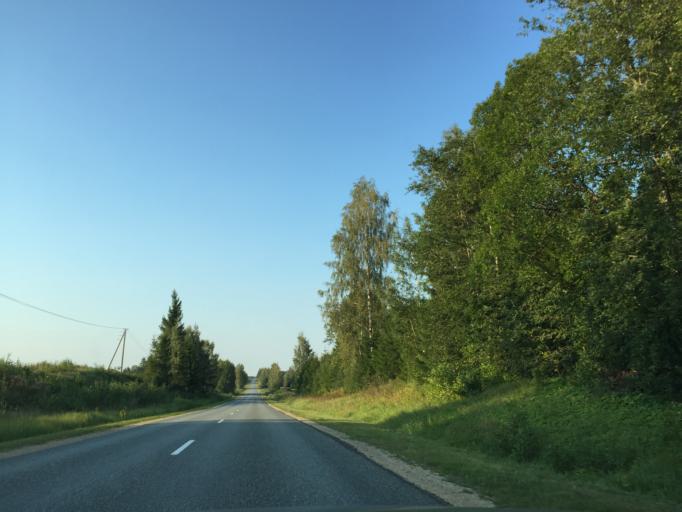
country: LV
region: Limbazu Rajons
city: Limbazi
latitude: 57.5616
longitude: 24.7658
